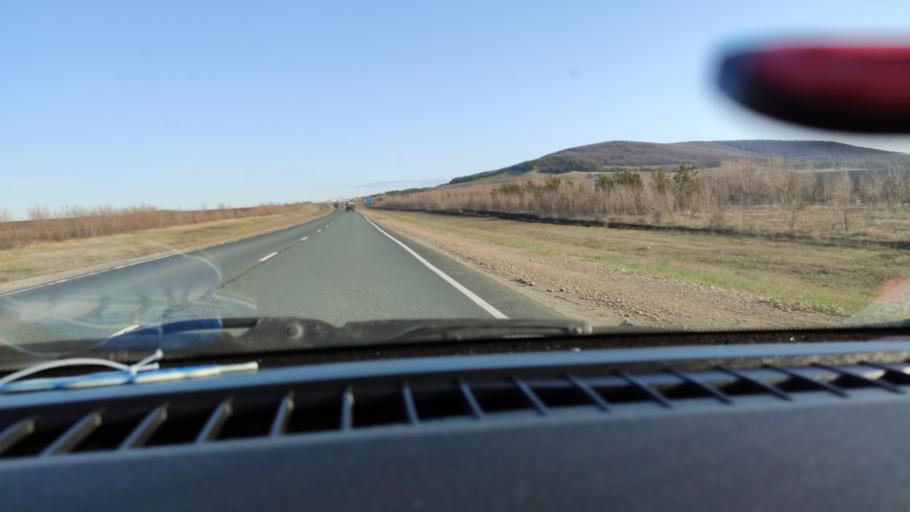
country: RU
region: Saratov
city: Alekseyevka
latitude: 52.2841
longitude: 47.9309
